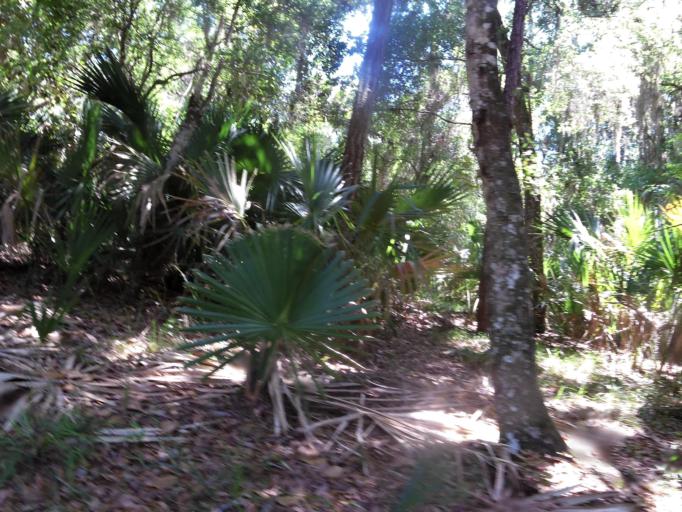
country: US
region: Florida
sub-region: Flagler County
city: Flagler Beach
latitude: 29.4349
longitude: -81.1382
